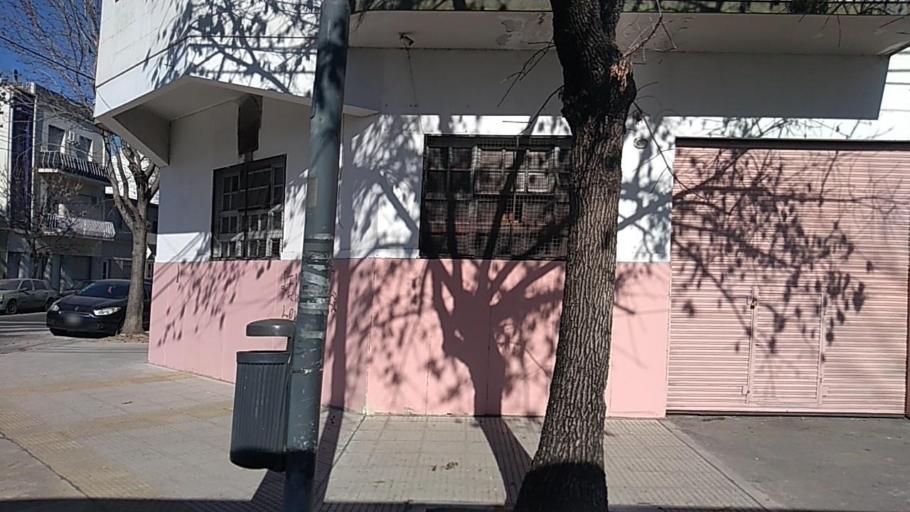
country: AR
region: Buenos Aires F.D.
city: Villa Santa Rita
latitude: -34.6190
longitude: -58.4956
